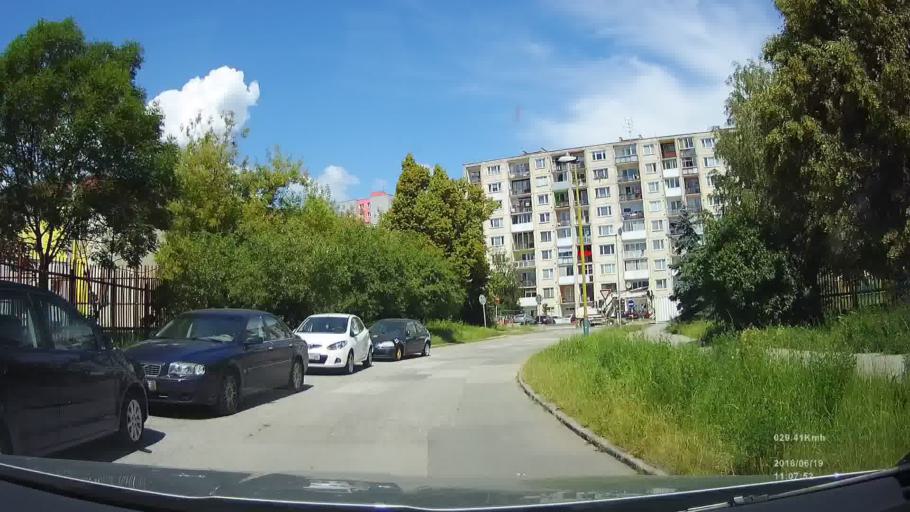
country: SK
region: Kosicky
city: Kosice
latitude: 48.7101
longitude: 21.2426
